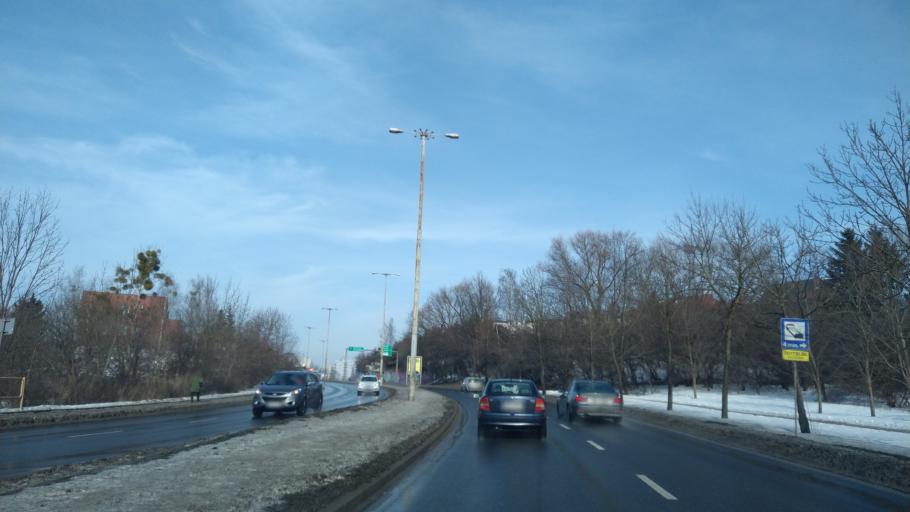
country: PL
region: Warmian-Masurian Voivodeship
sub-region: Powiat olsztynski
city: Olsztyn
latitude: 53.7592
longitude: 20.4999
